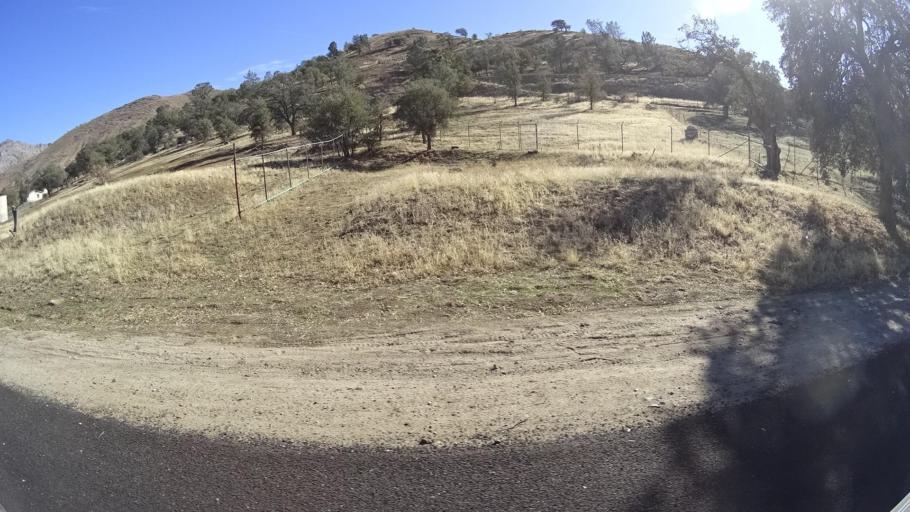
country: US
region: California
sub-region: Kern County
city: Bodfish
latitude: 35.5980
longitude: -118.4905
